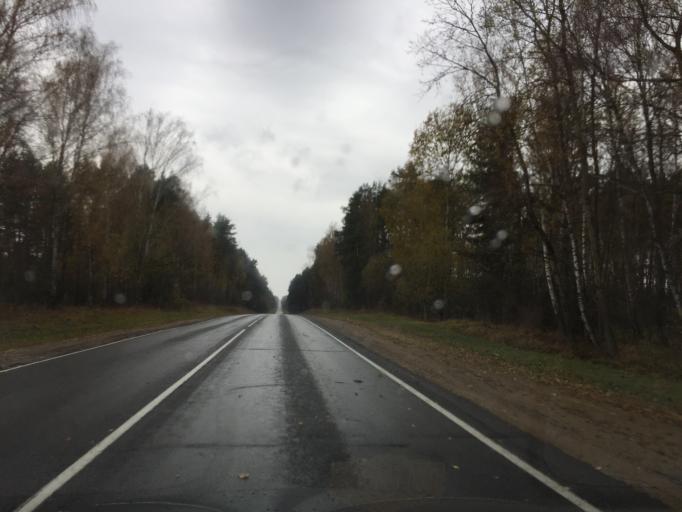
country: BY
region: Mogilev
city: Slawharad
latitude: 53.4154
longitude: 30.9515
